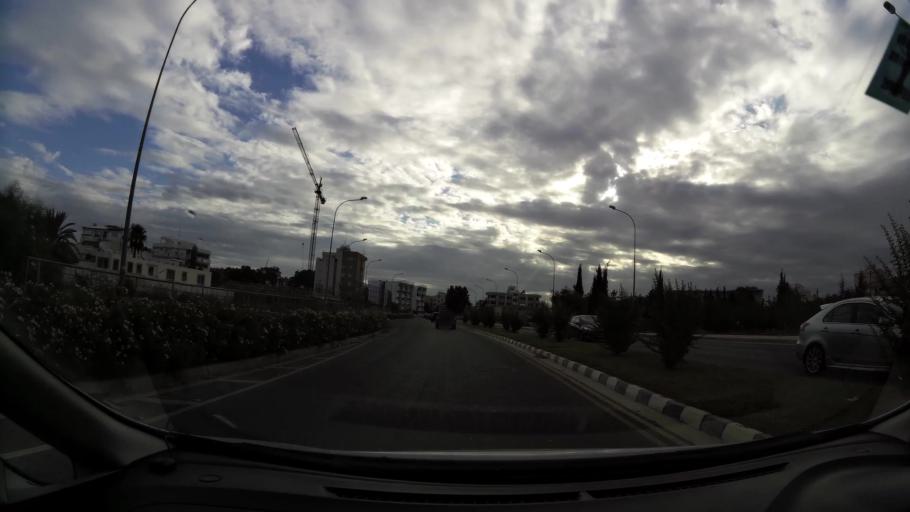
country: CY
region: Lefkosia
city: Nicosia
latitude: 35.1556
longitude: 33.3368
